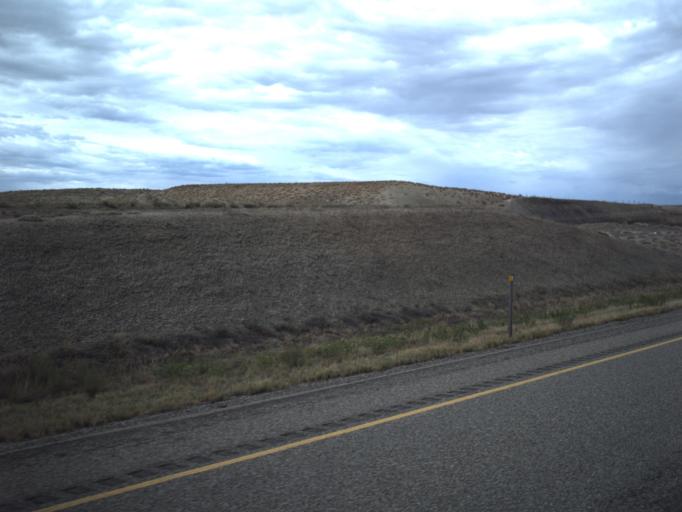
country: US
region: Colorado
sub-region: Mesa County
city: Loma
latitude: 39.1195
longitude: -109.1746
